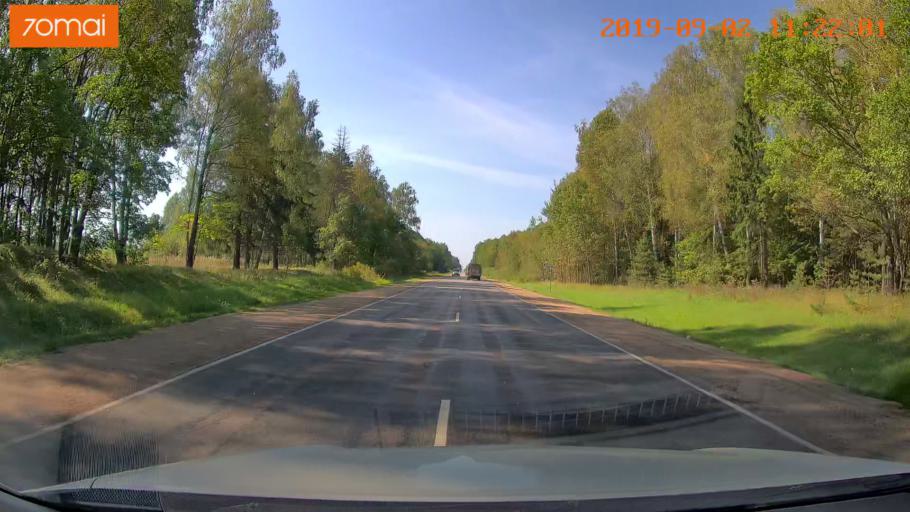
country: RU
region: Smolensk
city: Roslavl'
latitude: 54.0297
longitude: 33.0230
